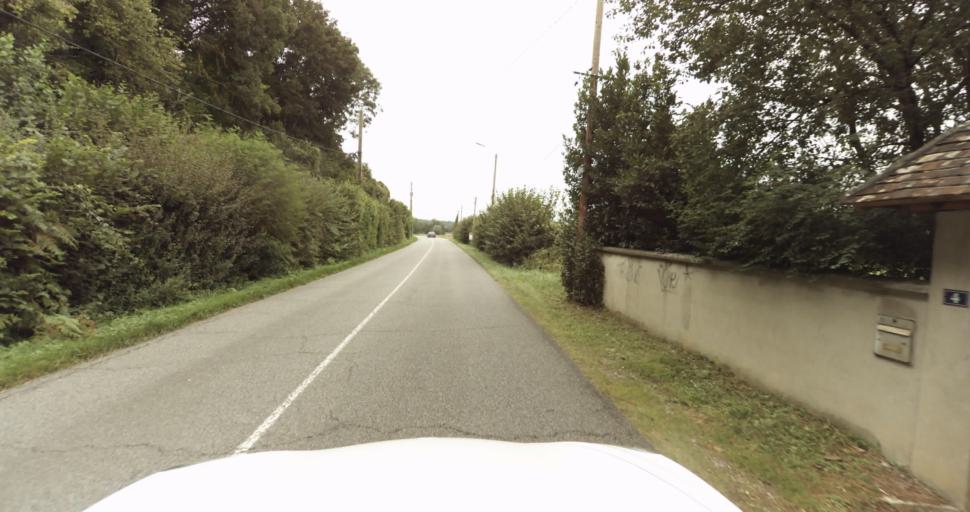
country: FR
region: Haute-Normandie
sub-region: Departement de l'Eure
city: Arnieres-sur-Iton
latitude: 49.0057
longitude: 1.1030
